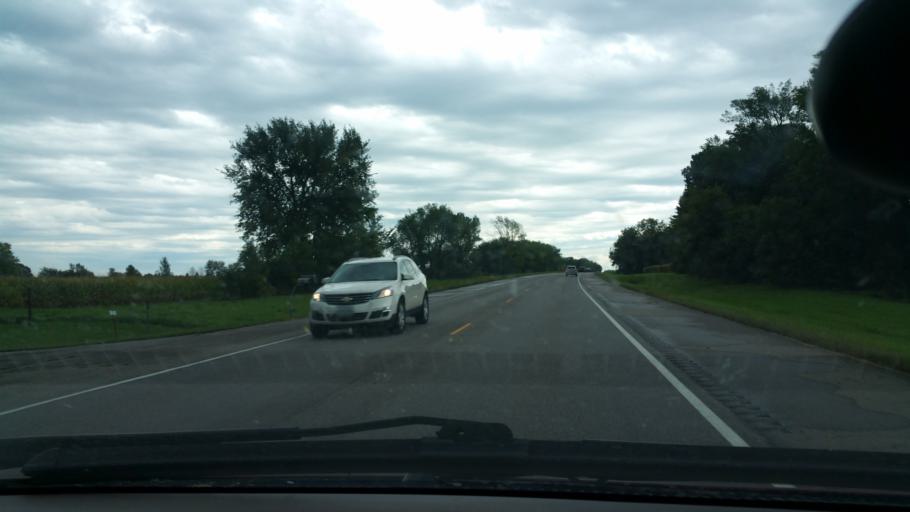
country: US
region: Minnesota
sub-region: Rice County
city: Dundas
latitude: 44.4716
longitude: -93.2360
